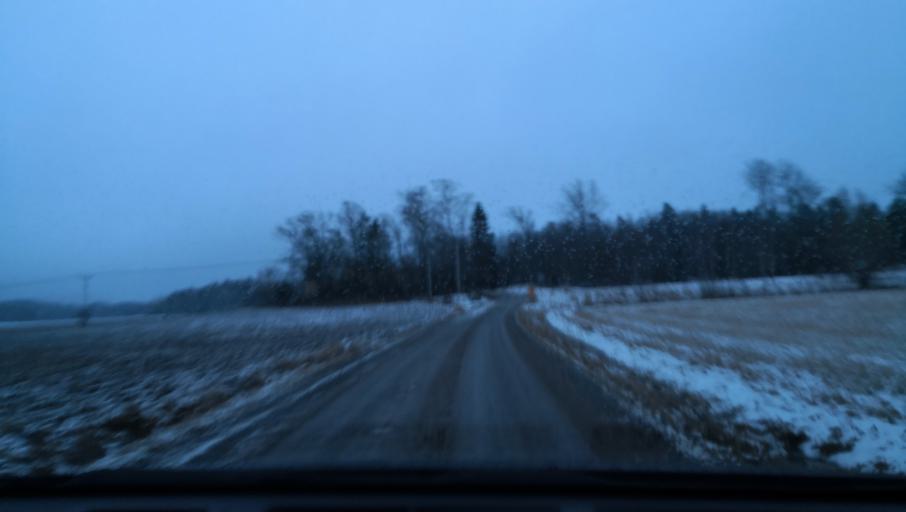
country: SE
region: Vaestmanland
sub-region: Kungsors Kommun
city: Kungsoer
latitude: 59.4081
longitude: 16.2029
